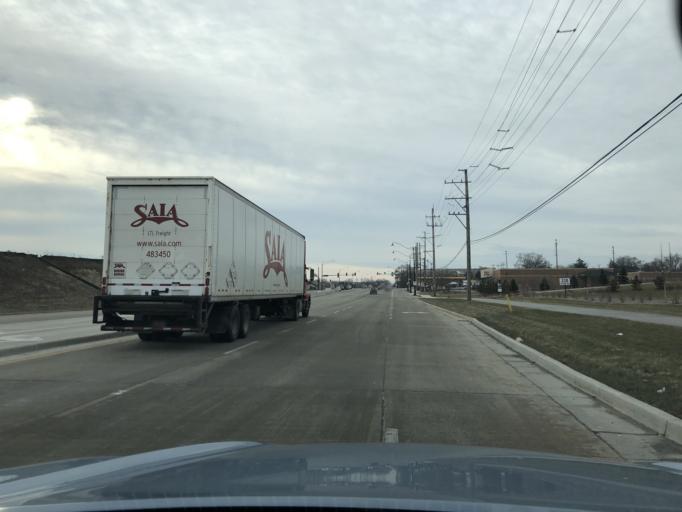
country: US
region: Illinois
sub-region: DuPage County
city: Bensenville
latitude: 41.9633
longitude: -87.9398
